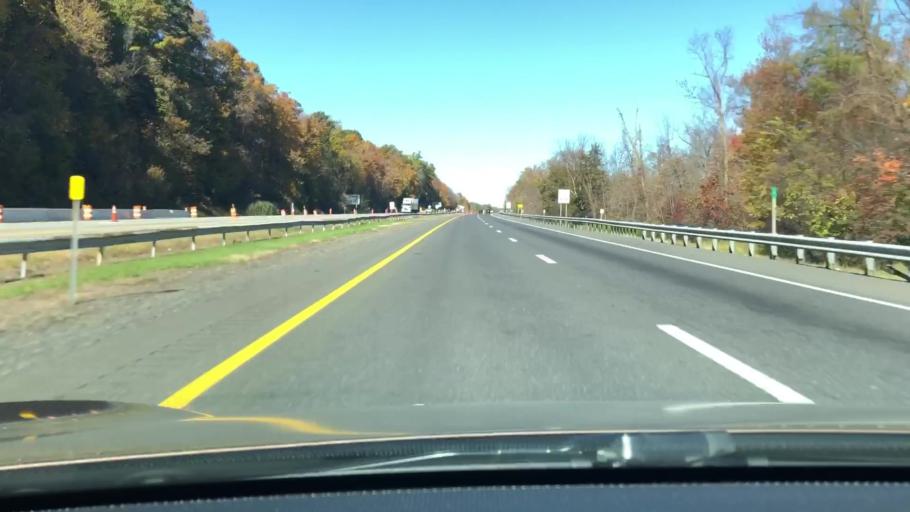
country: US
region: New York
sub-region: Orange County
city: Gardnertown
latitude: 41.5240
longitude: -74.0747
